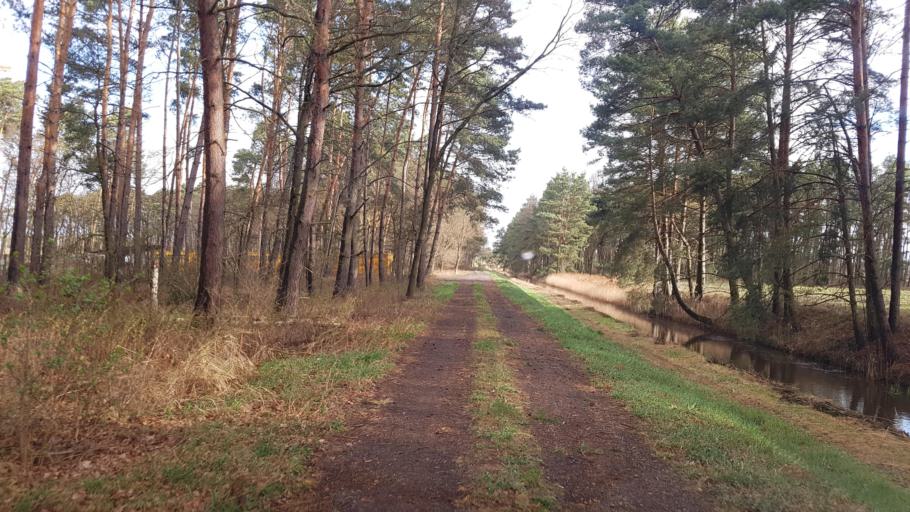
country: DE
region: Brandenburg
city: Bronkow
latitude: 51.6437
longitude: 13.8865
